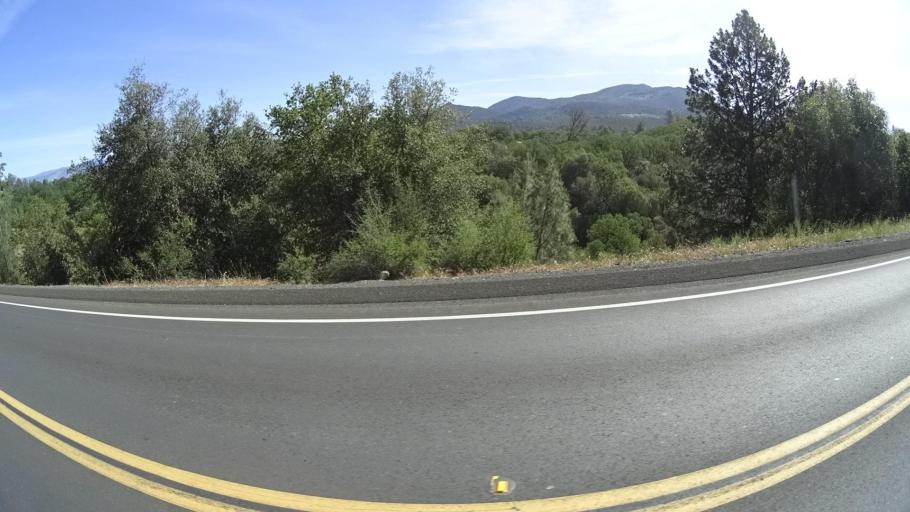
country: US
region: California
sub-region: Lake County
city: Kelseyville
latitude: 38.9624
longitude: -122.8287
